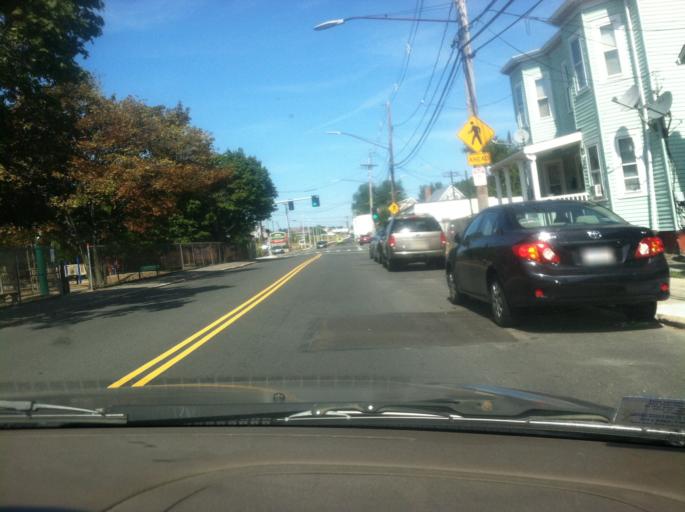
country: US
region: Massachusetts
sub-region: Suffolk County
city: Revere
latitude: 42.3873
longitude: -71.0082
